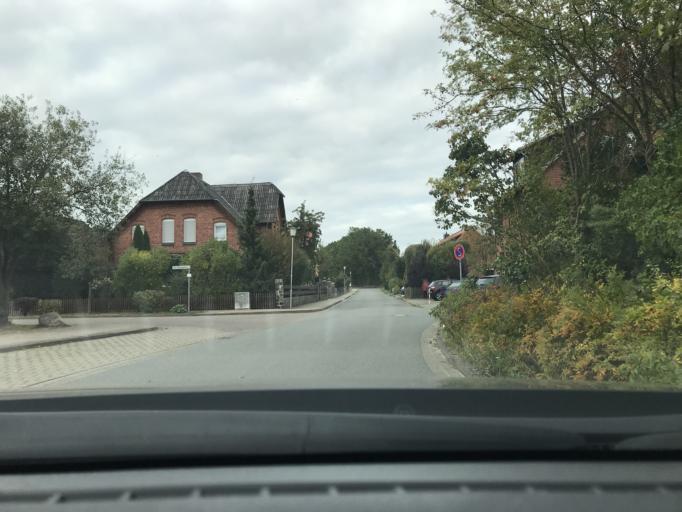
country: DE
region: Lower Saxony
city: Suderburg
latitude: 52.8982
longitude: 10.4500
